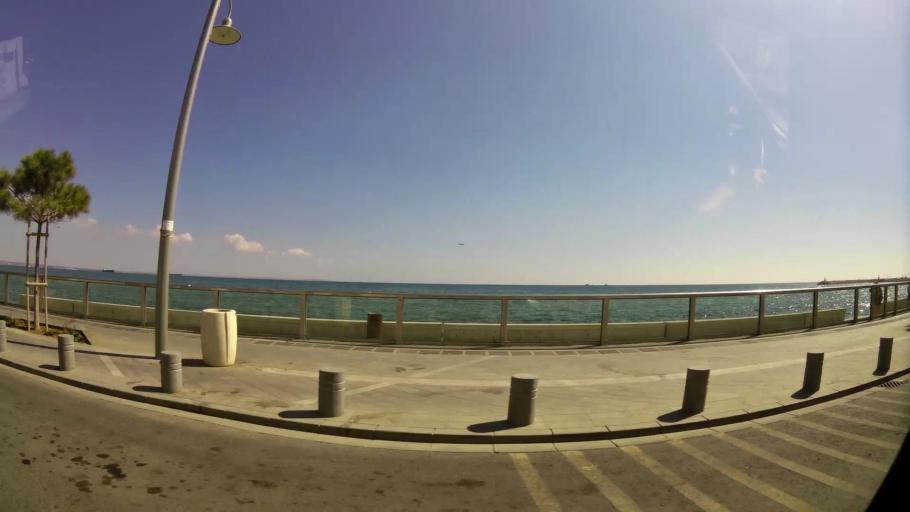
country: CY
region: Larnaka
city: Larnaca
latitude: 34.9029
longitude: 33.6377
